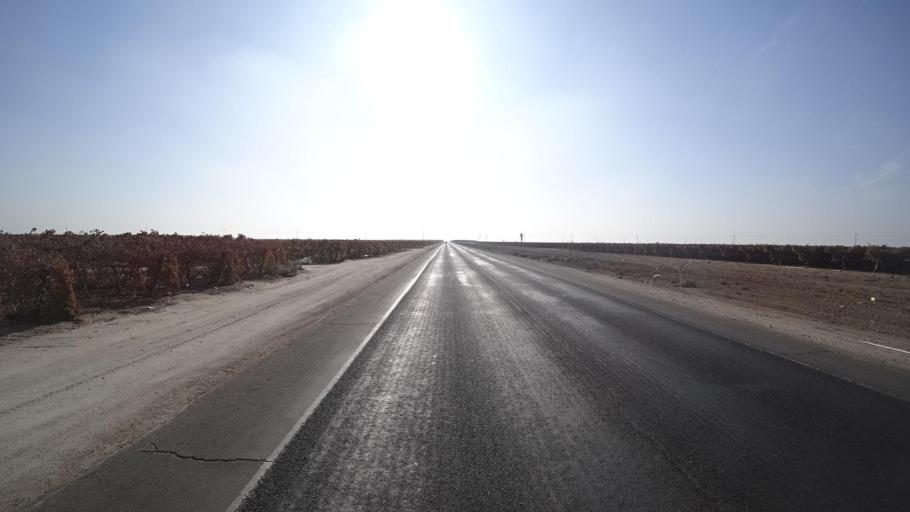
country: US
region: California
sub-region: Kern County
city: McFarland
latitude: 35.7078
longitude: -119.1659
